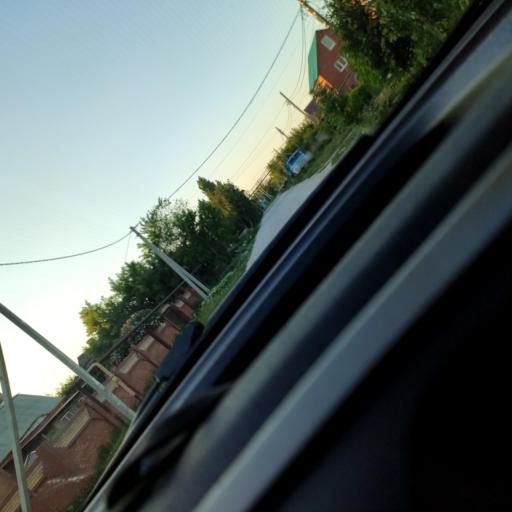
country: RU
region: Samara
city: Tol'yatti
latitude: 53.5538
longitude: 49.4041
